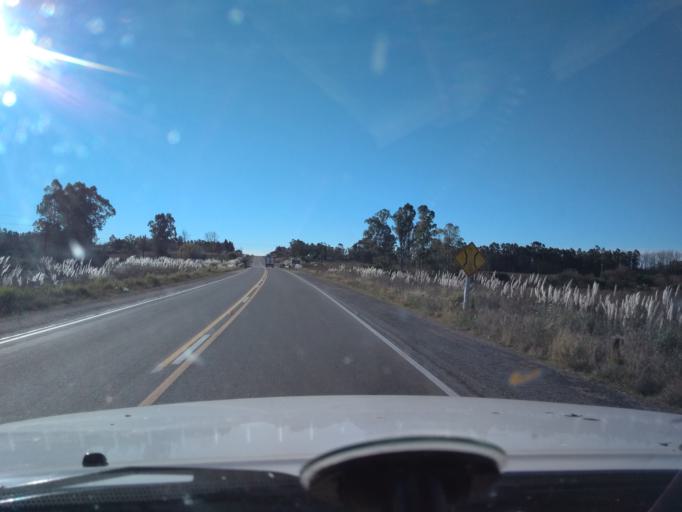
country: UY
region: Canelones
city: Sauce
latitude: -34.5957
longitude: -56.0513
